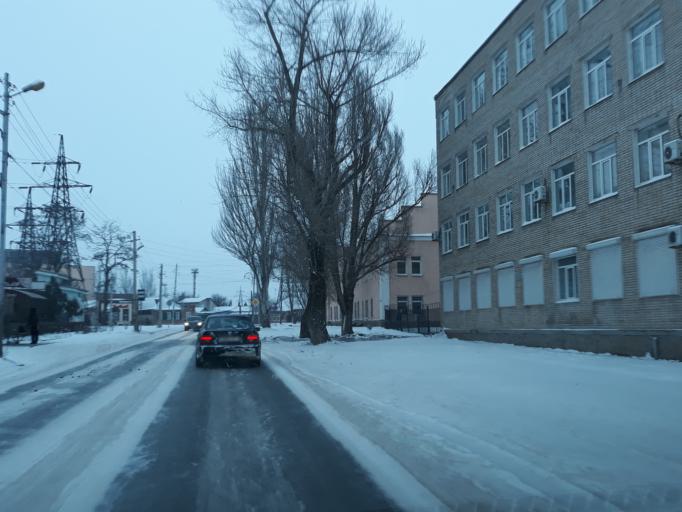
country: RU
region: Rostov
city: Taganrog
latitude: 47.2522
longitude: 38.9346
